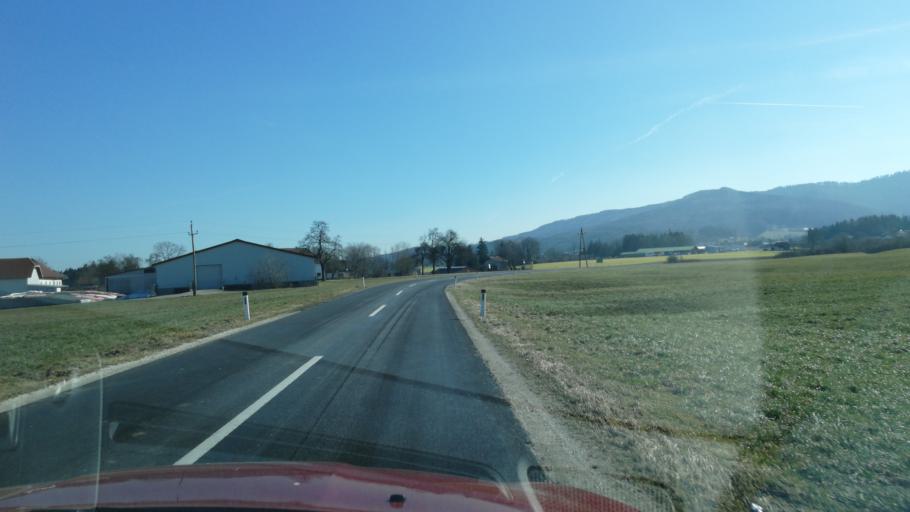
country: AT
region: Upper Austria
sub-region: Politischer Bezirk Vocklabruck
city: Aurach am Hongar
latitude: 47.9590
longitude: 13.6529
